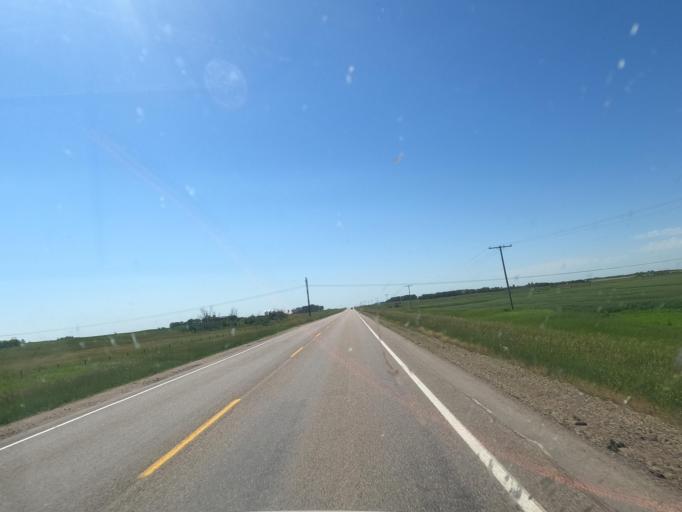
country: CA
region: Saskatchewan
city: Estevan
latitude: 49.6684
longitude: -102.9177
